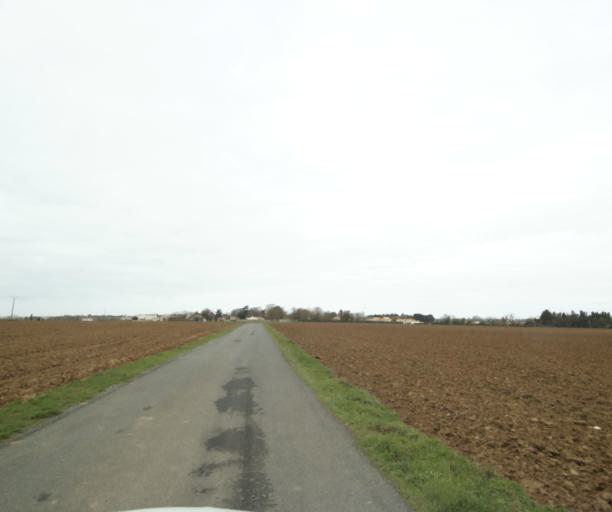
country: FR
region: Poitou-Charentes
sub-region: Departement de la Charente-Maritime
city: Nieul-sur-Mer
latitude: 46.1927
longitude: -1.1670
